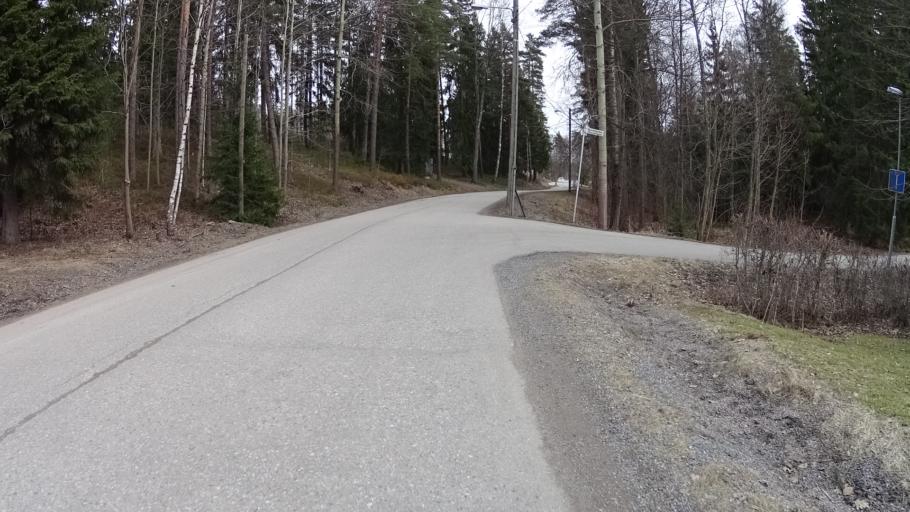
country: FI
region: Uusimaa
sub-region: Helsinki
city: Kauniainen
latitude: 60.2213
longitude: 24.7317
